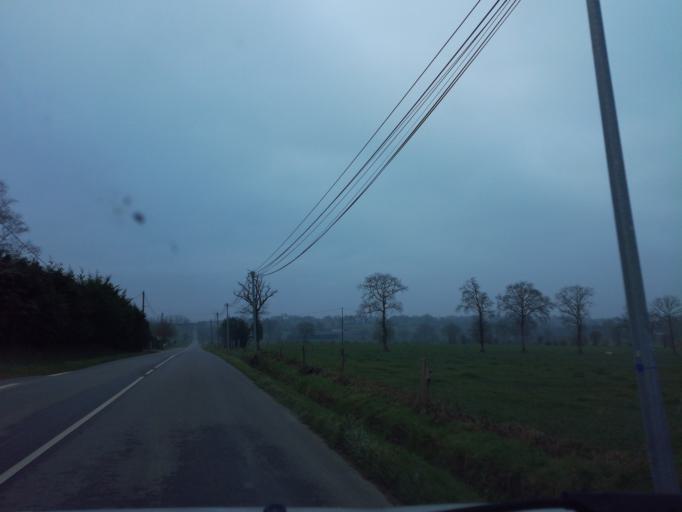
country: FR
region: Brittany
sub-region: Departement d'Ille-et-Vilaine
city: Gosne
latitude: 48.2584
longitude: -1.4525
